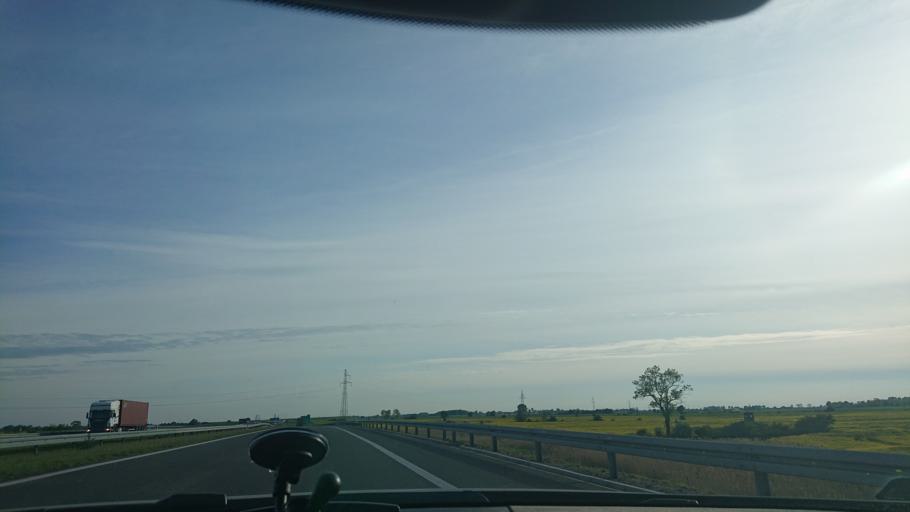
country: PL
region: Greater Poland Voivodeship
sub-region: Powiat gnieznienski
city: Gniezno
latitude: 52.5331
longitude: 17.5178
